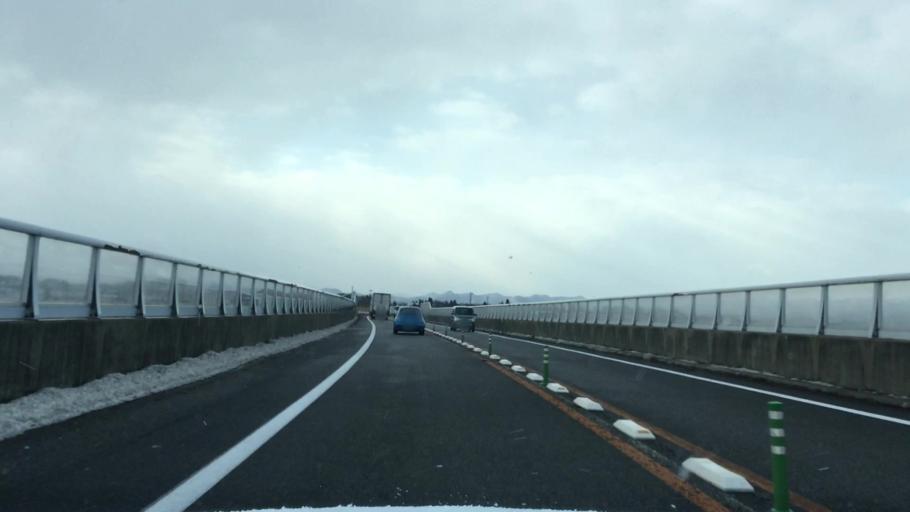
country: JP
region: Akita
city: Odate
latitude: 40.2862
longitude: 140.5412
